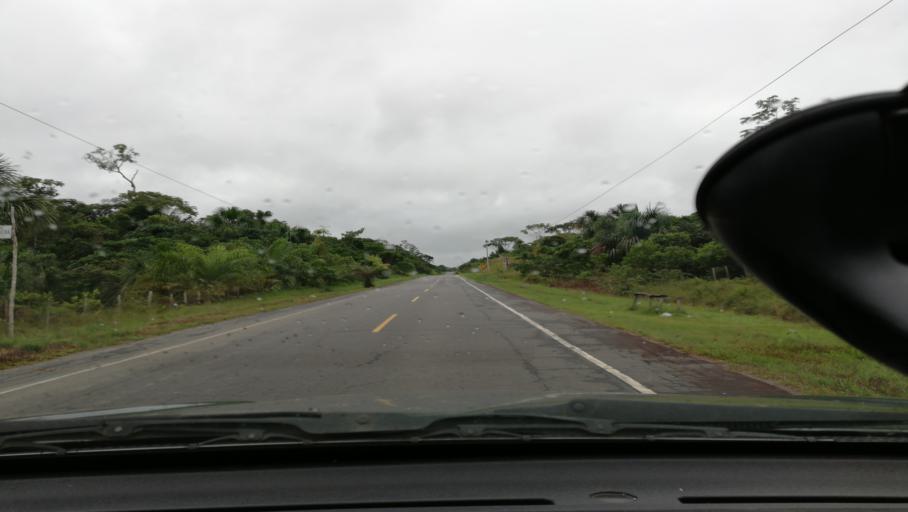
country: PE
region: Loreto
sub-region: Provincia de Loreto
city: Nauta
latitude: -4.3622
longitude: -73.5568
